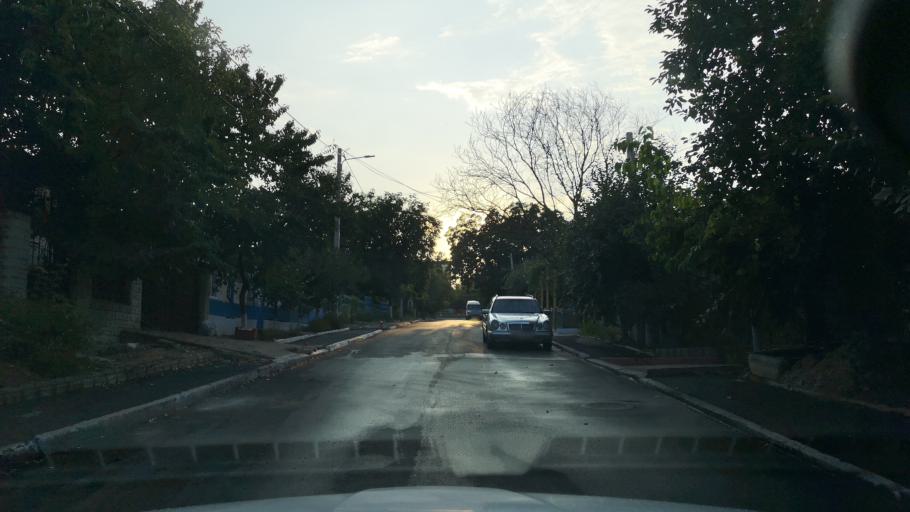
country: MD
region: Rezina
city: Rezina
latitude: 47.7531
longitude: 28.9582
